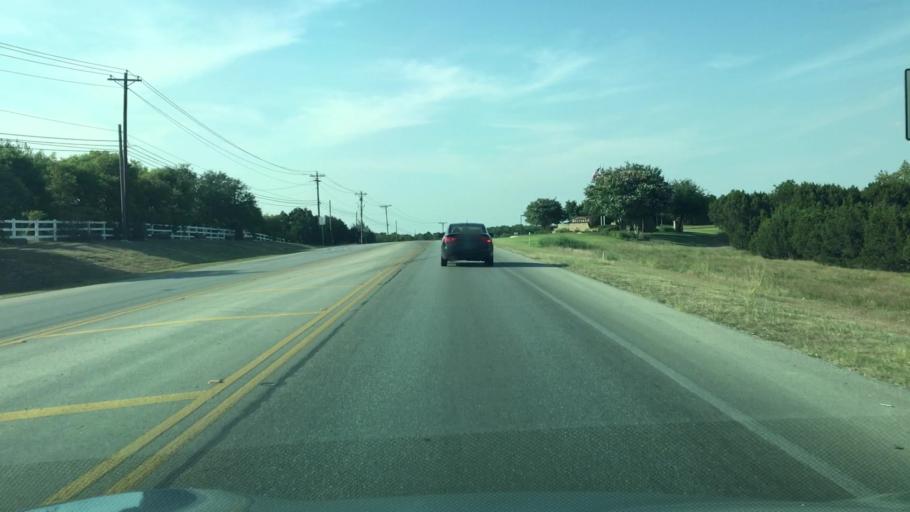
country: US
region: Texas
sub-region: Hays County
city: Dripping Springs
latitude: 30.1867
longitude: -98.0006
